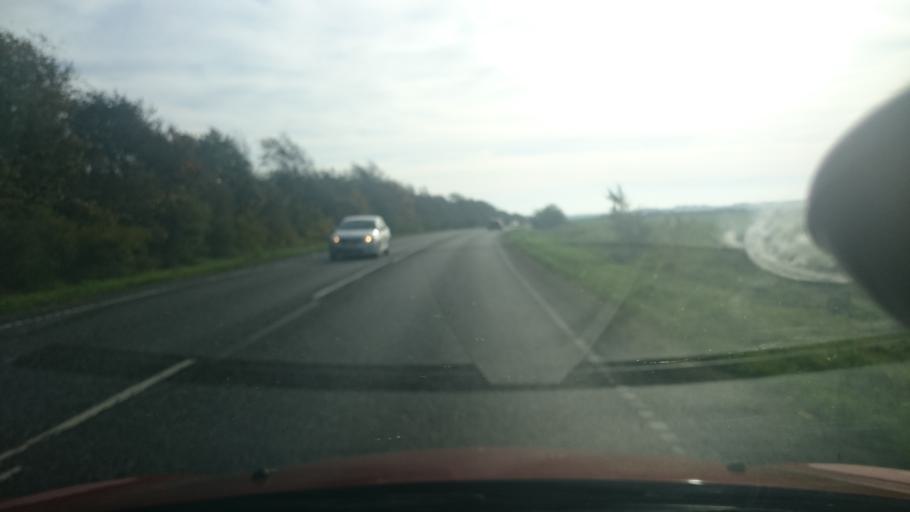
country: DK
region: Central Jutland
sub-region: Randers Kommune
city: Assentoft
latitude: 56.4392
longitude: 10.1227
